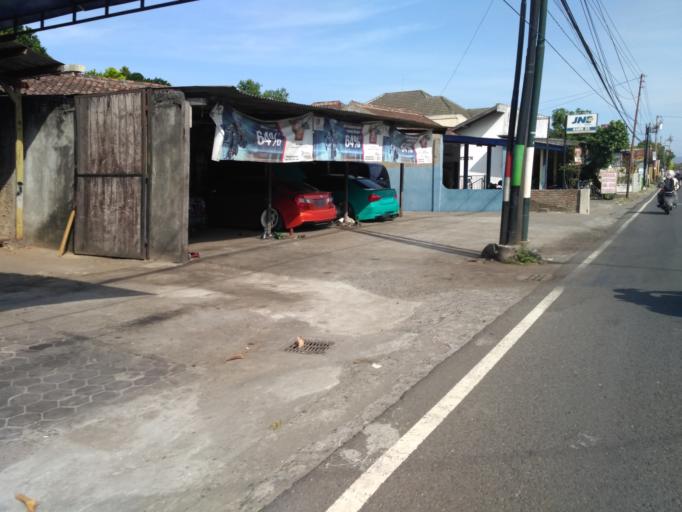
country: ID
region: Daerah Istimewa Yogyakarta
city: Depok
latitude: -7.7761
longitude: 110.4306
